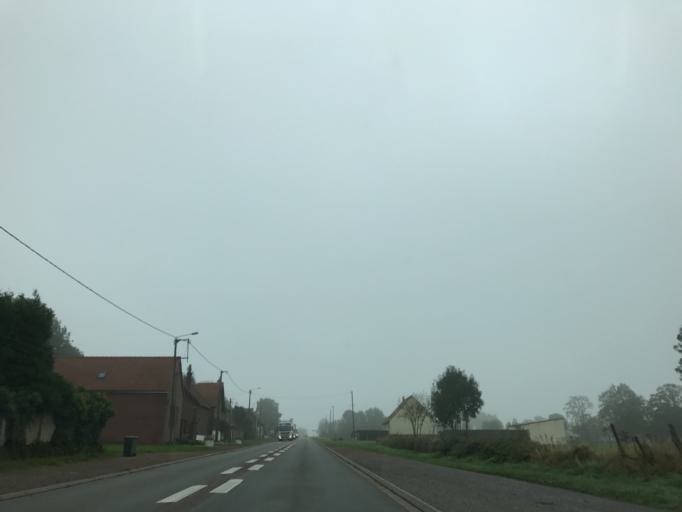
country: FR
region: Nord-Pas-de-Calais
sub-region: Departement du Pas-de-Calais
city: Bapaume
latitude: 50.0636
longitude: 2.8928
